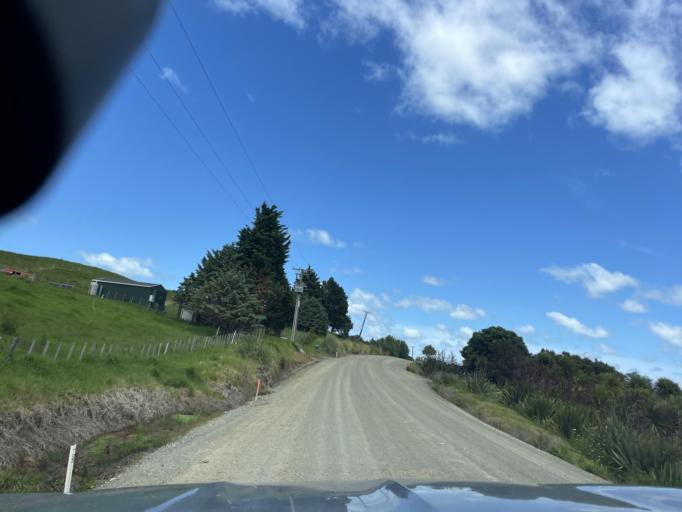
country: NZ
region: Auckland
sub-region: Auckland
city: Wellsford
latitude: -36.1680
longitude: 174.2802
